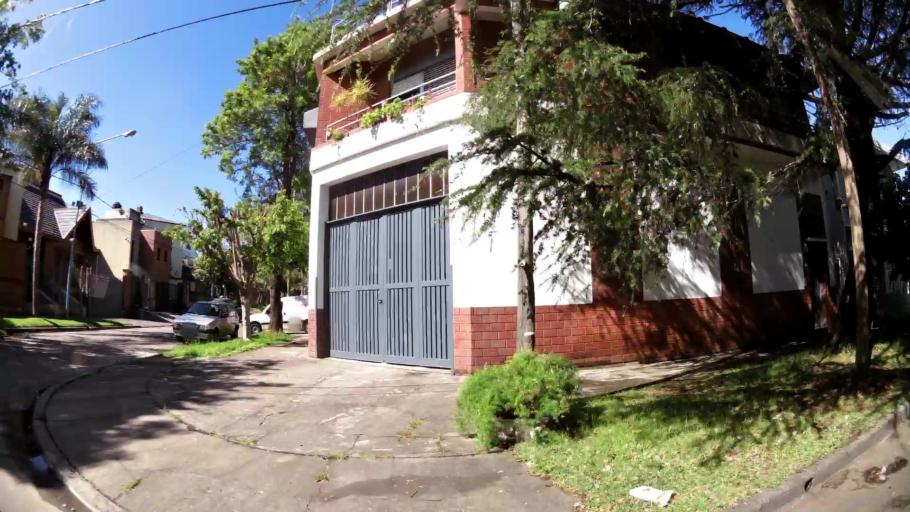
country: AR
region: Buenos Aires
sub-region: Partido de Quilmes
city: Quilmes
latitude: -34.6992
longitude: -58.2990
